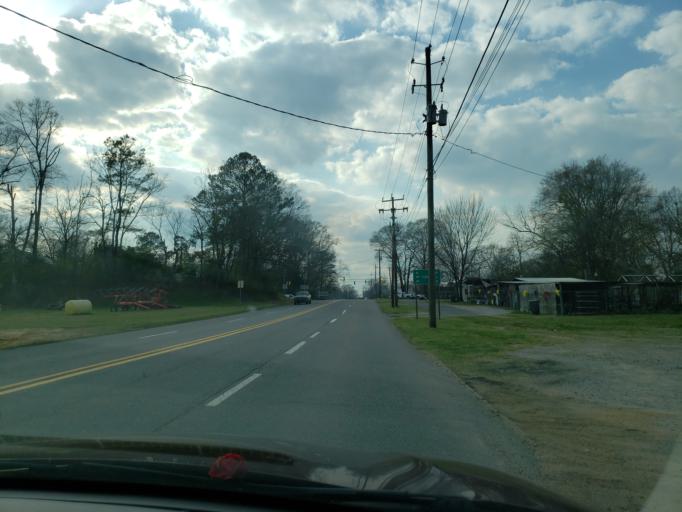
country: US
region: Alabama
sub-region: Hale County
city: Greensboro
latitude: 32.7000
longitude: -87.5985
